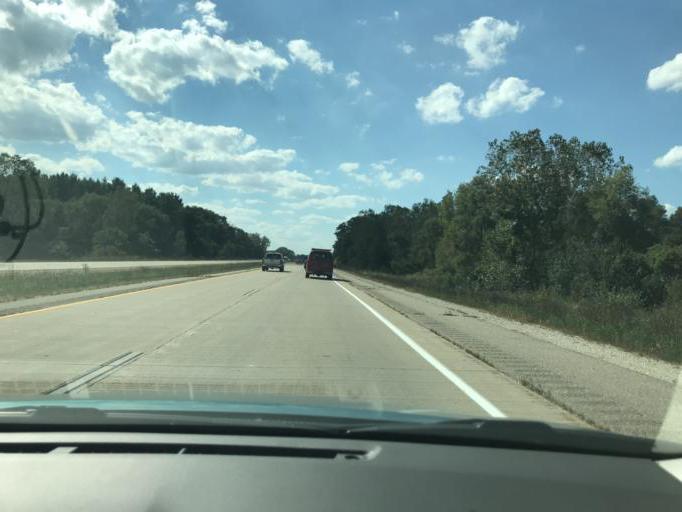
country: US
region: Wisconsin
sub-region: Kenosha County
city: Twin Lakes
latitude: 42.5827
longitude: -88.2227
